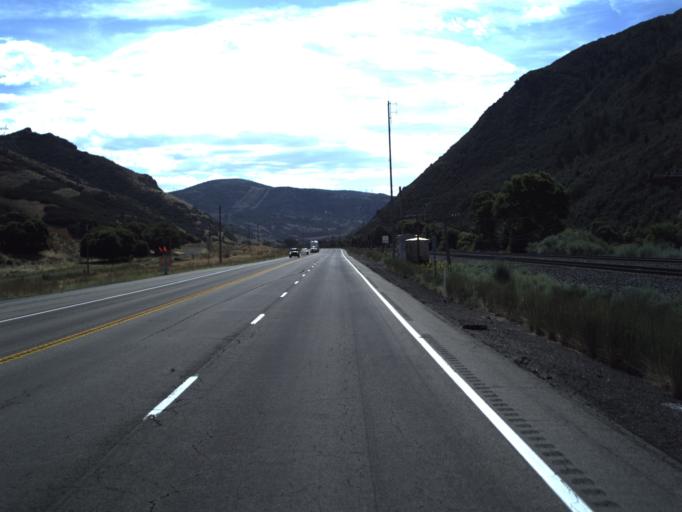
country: US
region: Utah
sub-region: Utah County
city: Mapleton
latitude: 40.0410
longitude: -111.5418
